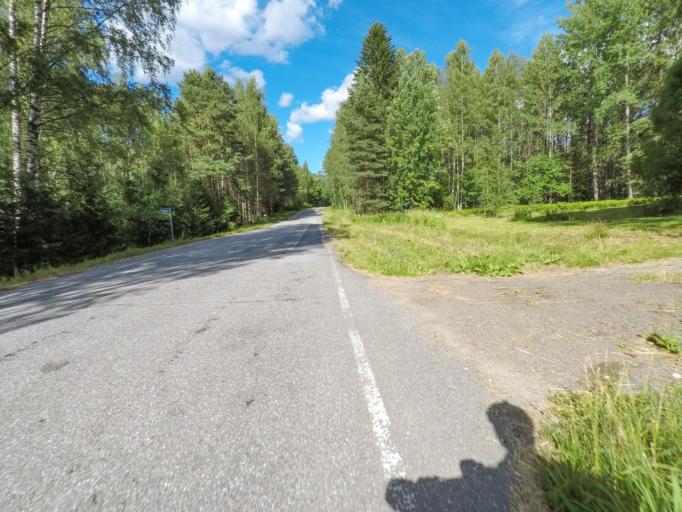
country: FI
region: South Karelia
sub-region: Lappeenranta
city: Joutseno
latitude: 61.1225
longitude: 28.3863
